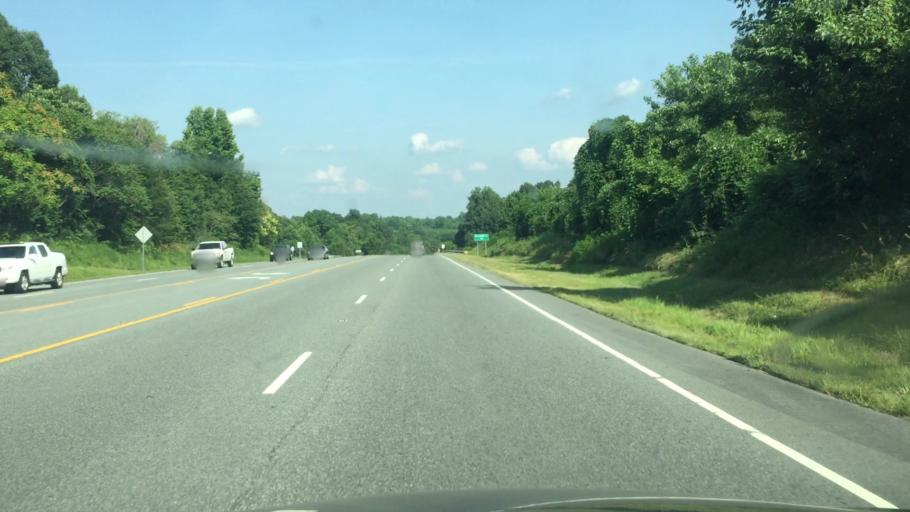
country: US
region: North Carolina
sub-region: Rockingham County
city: Reidsville
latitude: 36.3762
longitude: -79.6558
